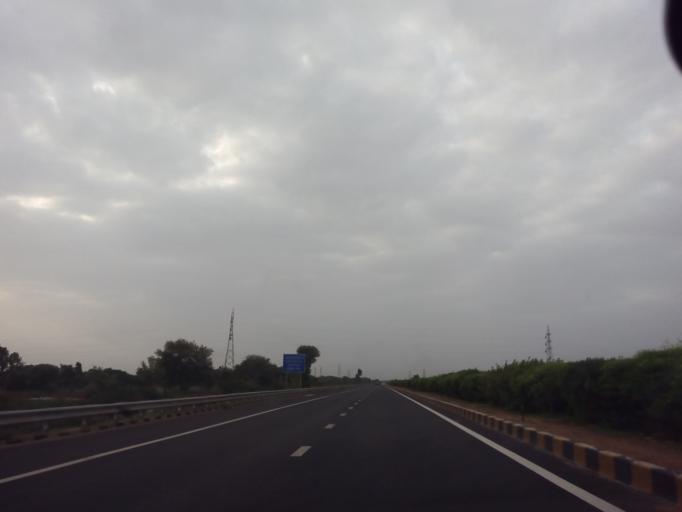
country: IN
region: Gujarat
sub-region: Kheda
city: Mahemdavad
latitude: 22.9432
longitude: 72.7096
